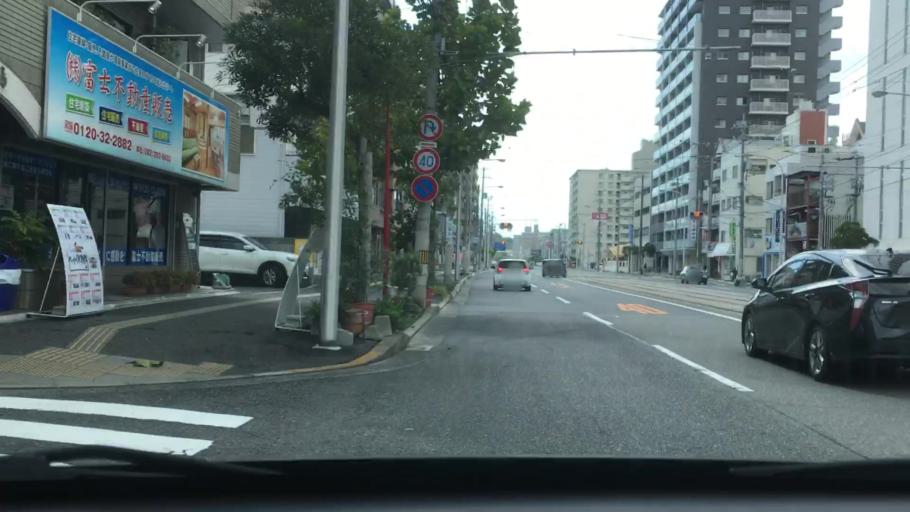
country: JP
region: Hiroshima
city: Hiroshima-shi
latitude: 34.3787
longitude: 132.4387
